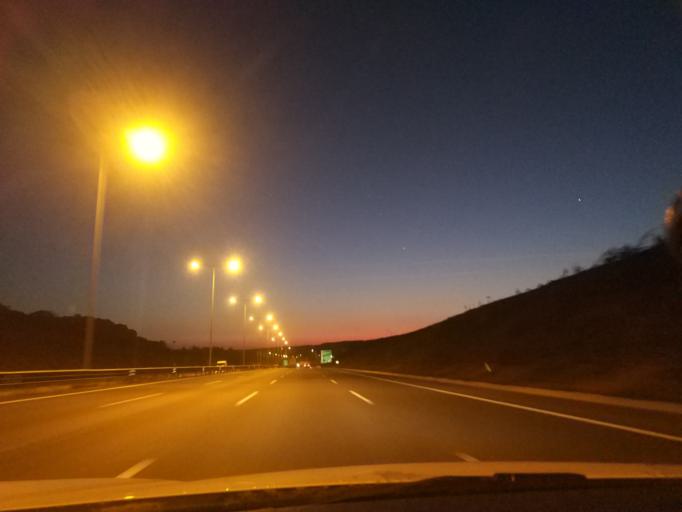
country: TR
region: Istanbul
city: Sancaktepe
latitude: 41.0470
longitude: 29.2618
